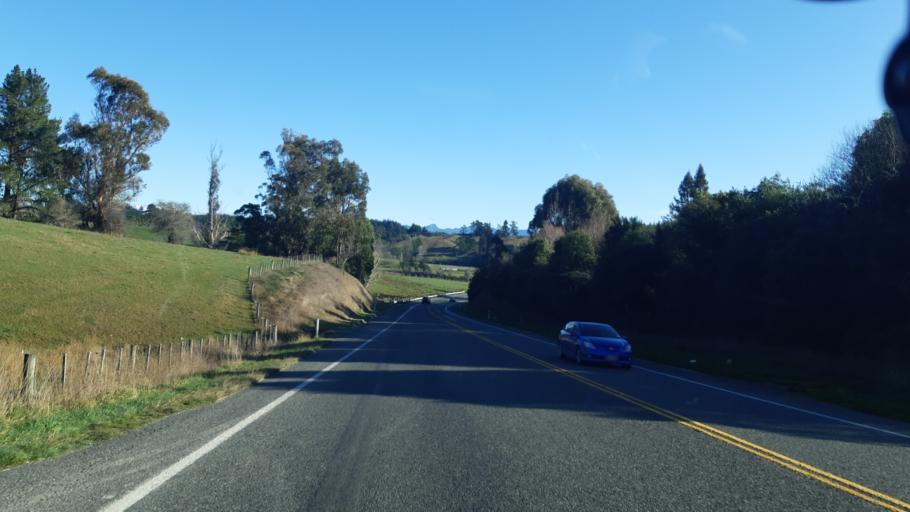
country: NZ
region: Tasman
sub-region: Tasman District
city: Mapua
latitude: -41.2829
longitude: 173.0745
